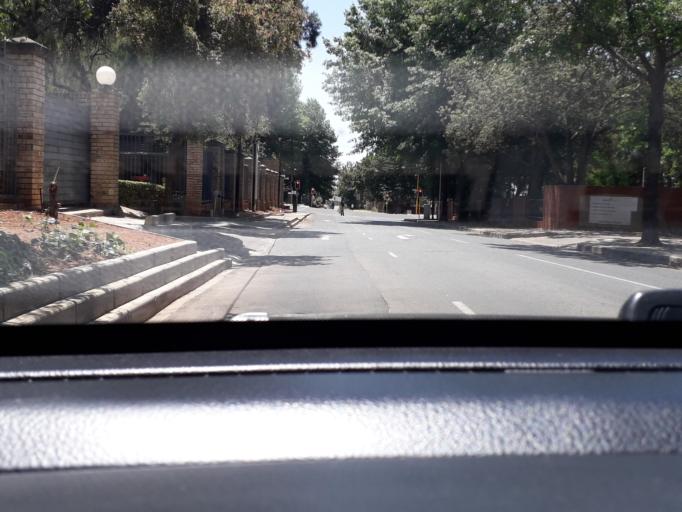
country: ZA
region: Gauteng
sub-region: City of Johannesburg Metropolitan Municipality
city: Modderfontein
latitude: -26.1009
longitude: 28.0636
